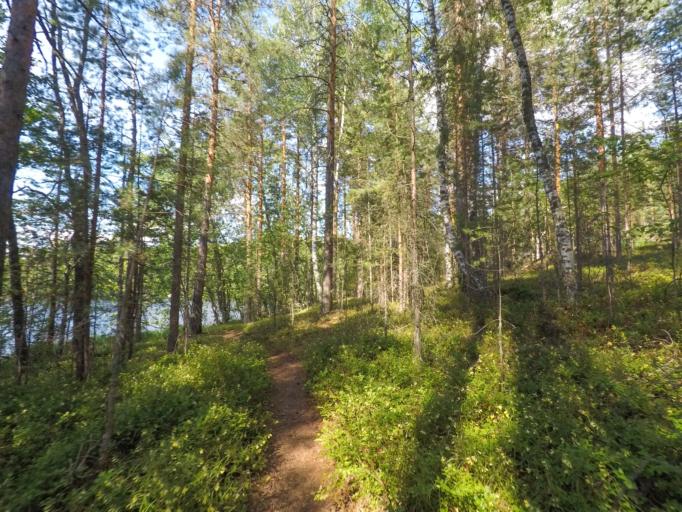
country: FI
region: Southern Savonia
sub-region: Mikkeli
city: Puumala
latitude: 61.4925
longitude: 28.1670
